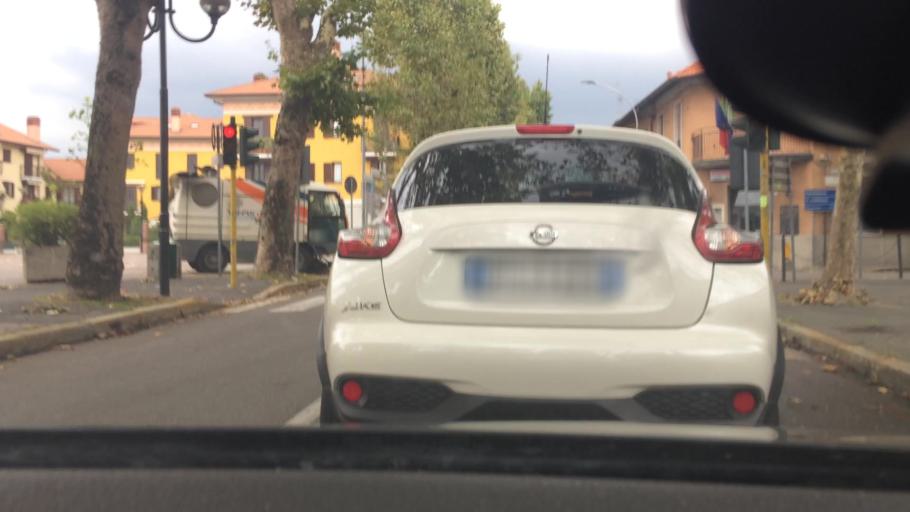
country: IT
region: Lombardy
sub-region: Citta metropolitana di Milano
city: Cantalupo
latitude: 45.5783
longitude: 8.9797
